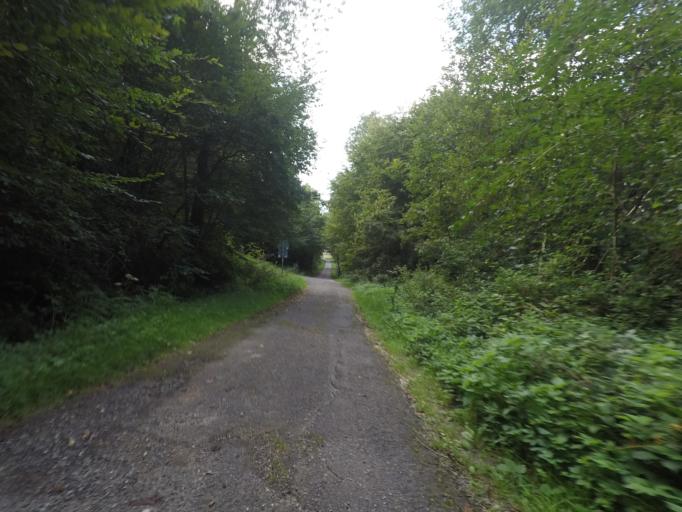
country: DE
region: Baden-Wuerttemberg
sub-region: Regierungsbezirk Stuttgart
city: Winterbach
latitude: 48.7870
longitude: 9.4601
